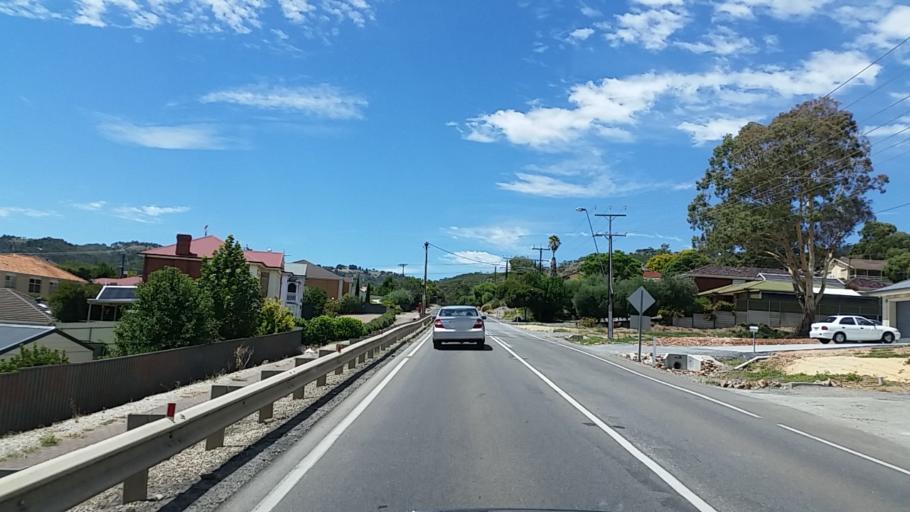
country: AU
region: South Australia
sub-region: Campbelltown
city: Athelstone
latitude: -34.8647
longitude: 138.7100
